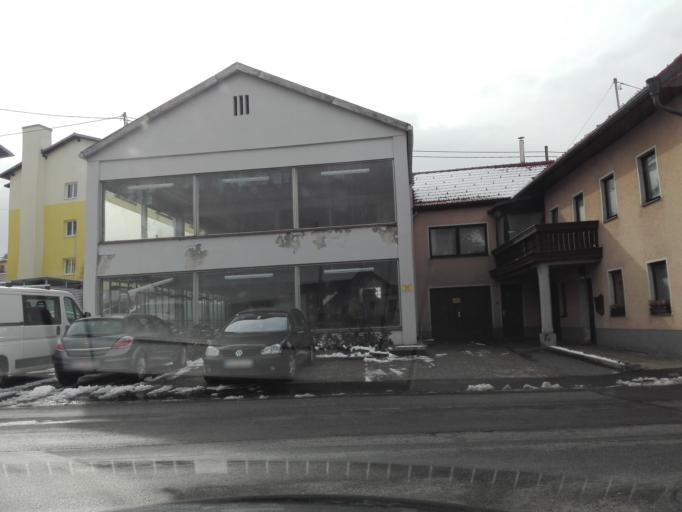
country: AT
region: Upper Austria
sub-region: Politischer Bezirk Rohrbach
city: Atzesberg
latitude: 48.4965
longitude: 13.8930
